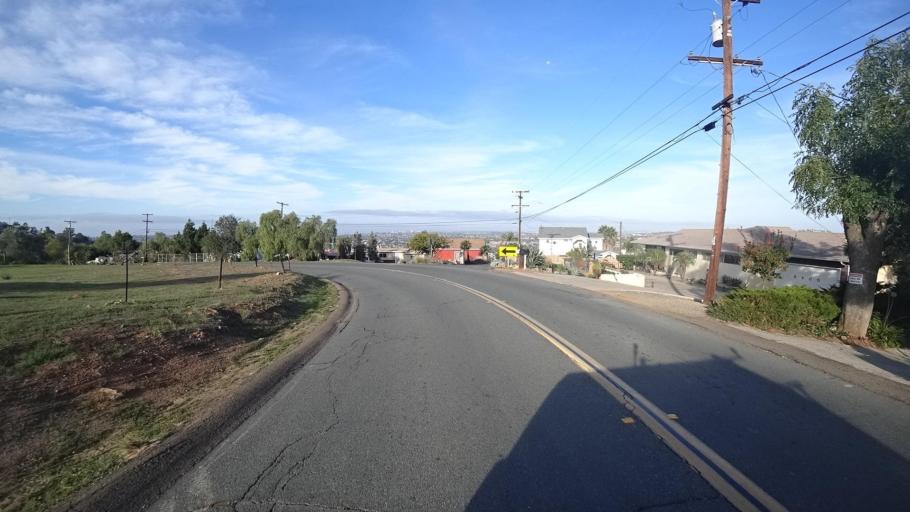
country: US
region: California
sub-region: San Diego County
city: Spring Valley
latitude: 32.7313
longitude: -116.9956
